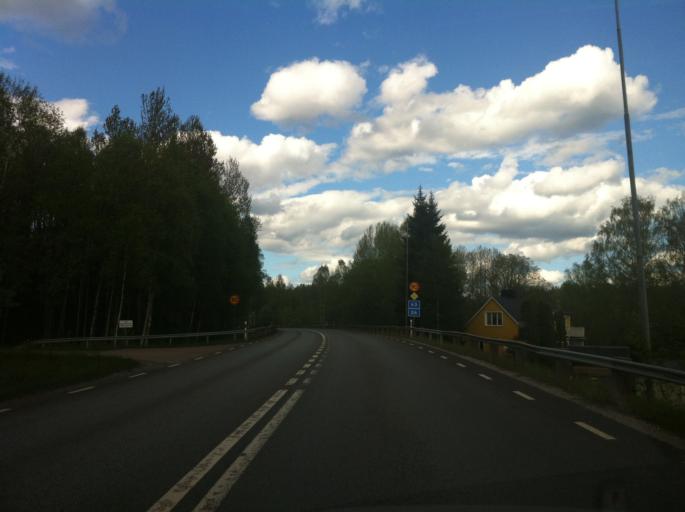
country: SE
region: Vaermland
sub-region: Filipstads Kommun
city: Filipstad
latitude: 59.7496
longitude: 14.2388
